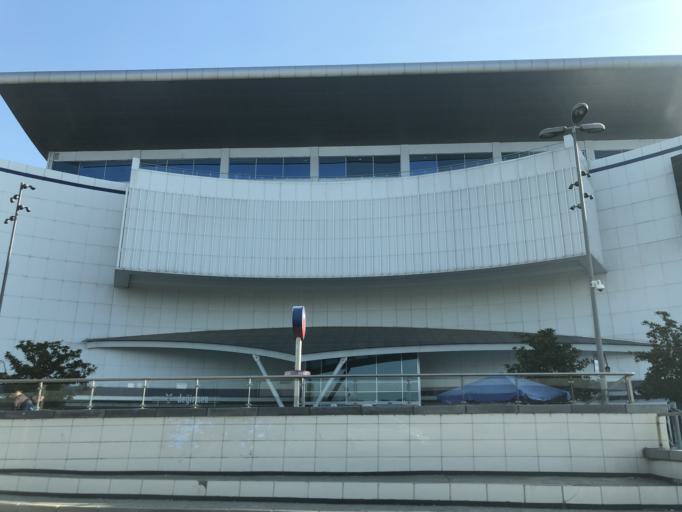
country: TR
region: Istanbul
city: UEskuedar
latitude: 41.0003
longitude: 29.0304
